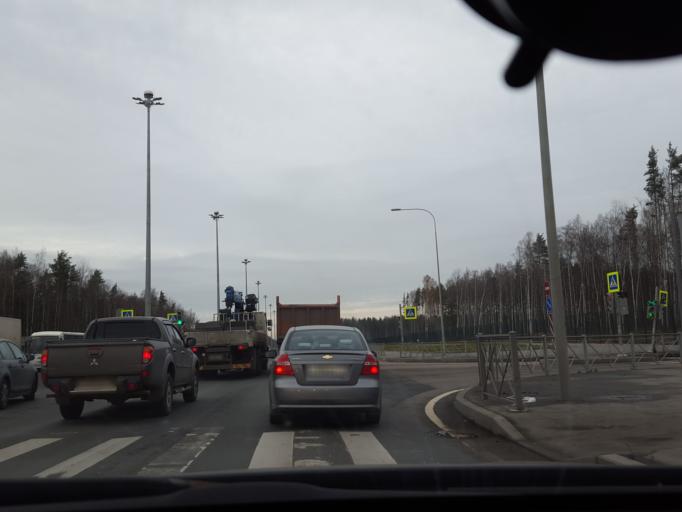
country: RU
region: Leningrad
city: Untolovo
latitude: 60.0479
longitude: 30.2330
